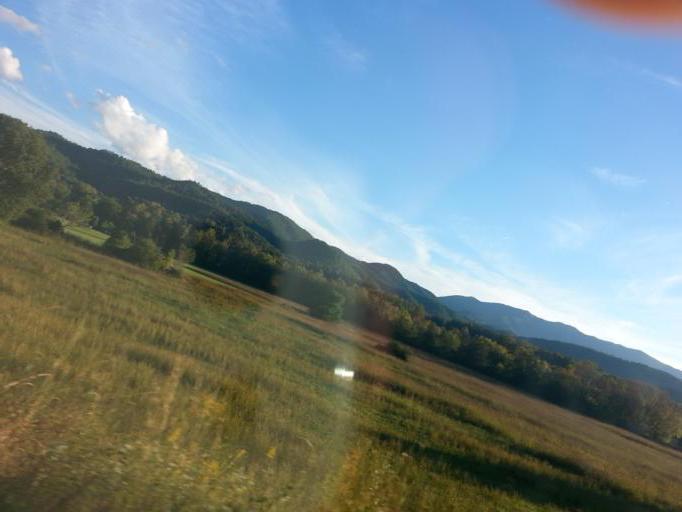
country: US
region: Tennessee
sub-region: Blount County
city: Wildwood
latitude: 35.6836
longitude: -83.7296
